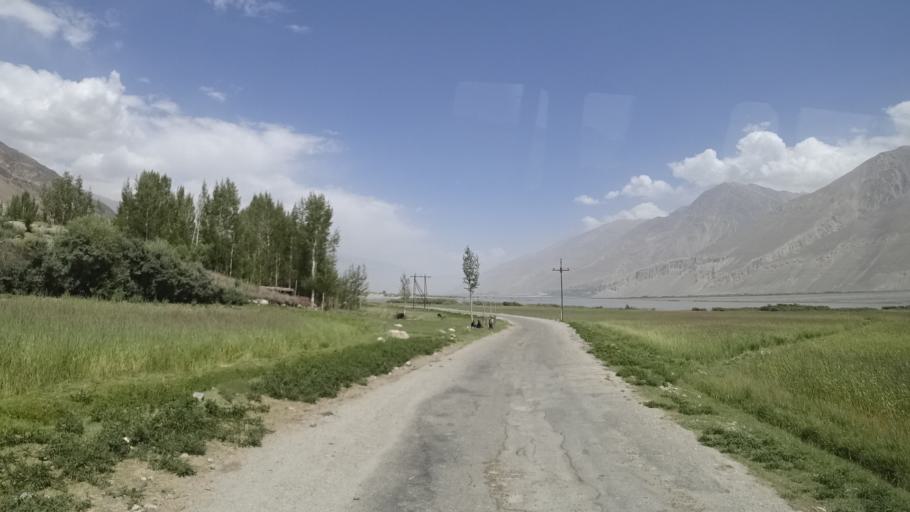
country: AF
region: Badakhshan
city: Khandud
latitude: 36.9266
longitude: 72.2009
